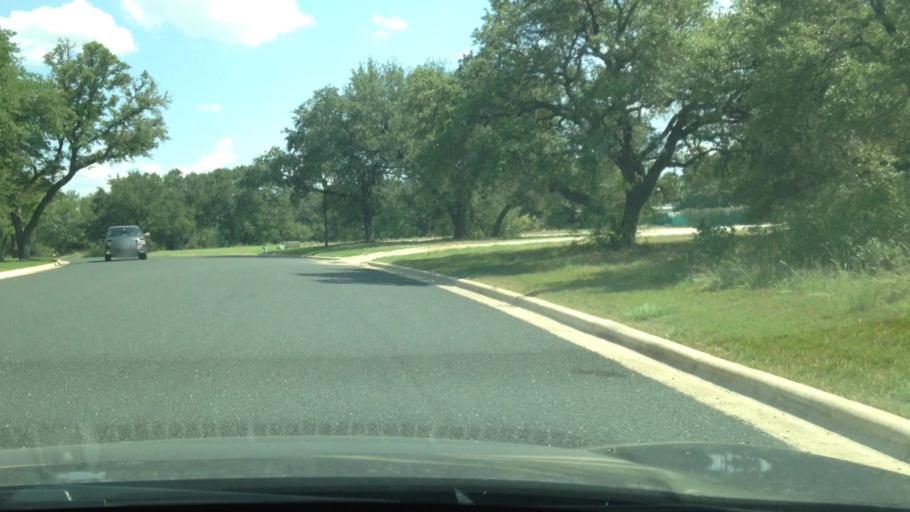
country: US
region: Texas
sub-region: Williamson County
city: Leander
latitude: 30.6390
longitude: -97.7965
